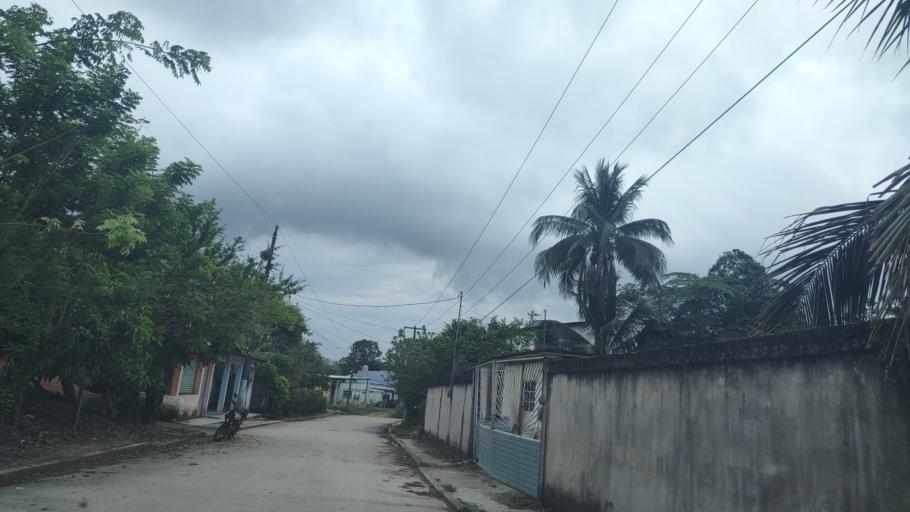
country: MX
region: Veracruz
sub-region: Uxpanapa
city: Poblado 10
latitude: 17.4984
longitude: -94.1627
